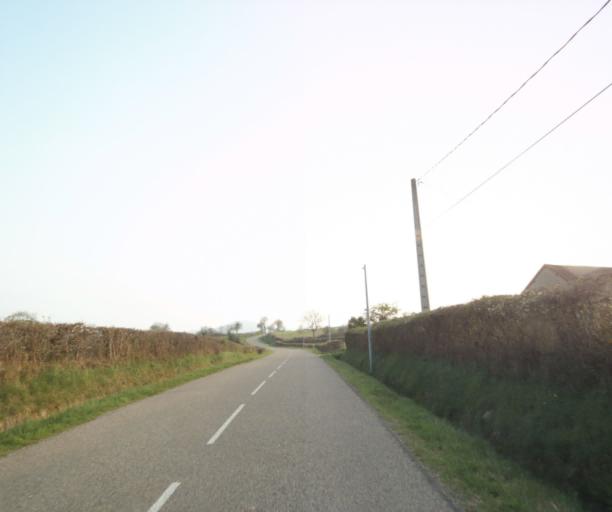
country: FR
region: Bourgogne
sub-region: Departement de Saone-et-Loire
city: Charolles
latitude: 46.4512
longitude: 4.4300
